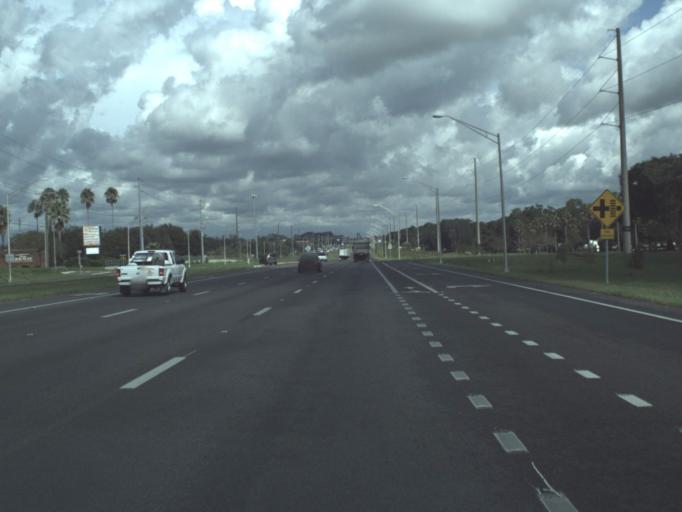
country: US
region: Florida
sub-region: Polk County
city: Highland City
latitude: 27.9792
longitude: -81.8874
